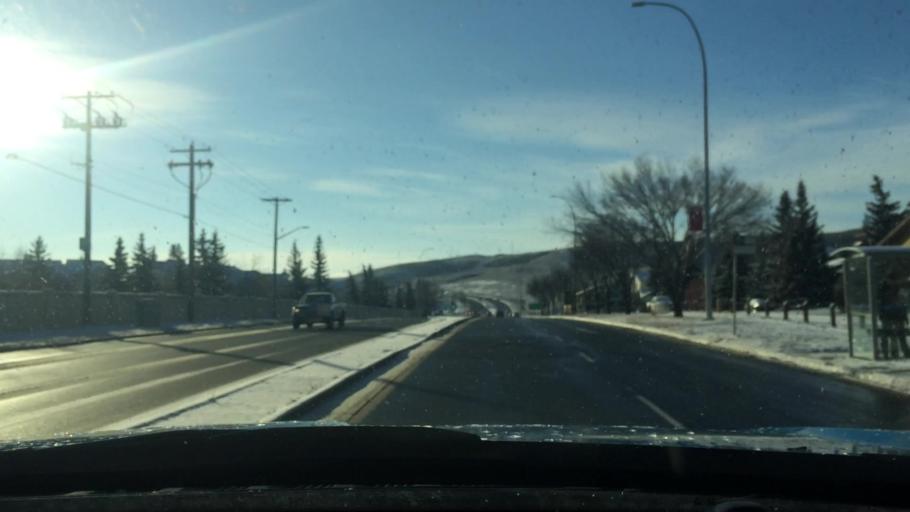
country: CA
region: Alberta
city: Calgary
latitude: 51.1346
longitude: -114.1072
